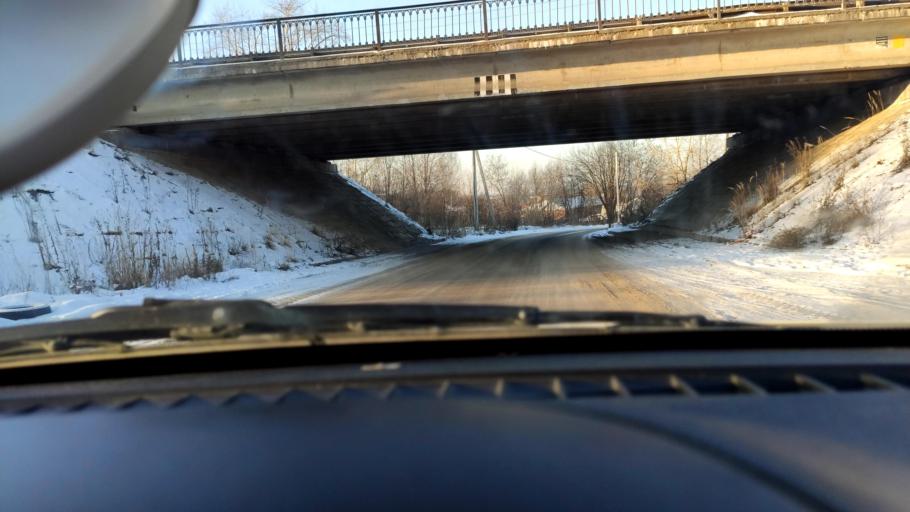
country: RU
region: Perm
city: Perm
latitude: 58.0707
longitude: 56.3677
